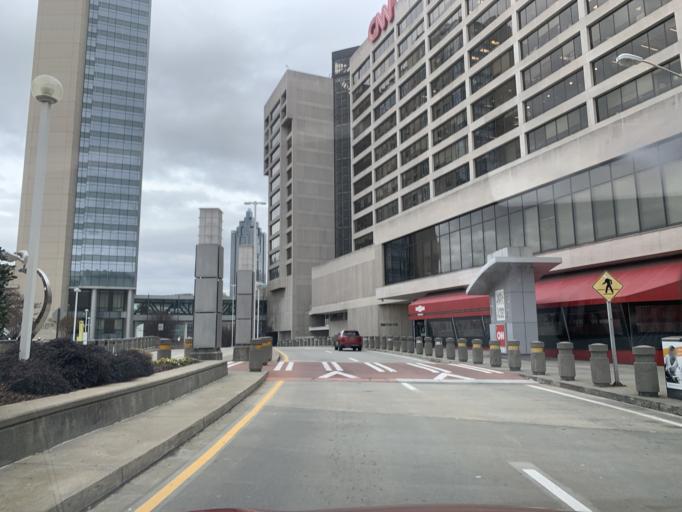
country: US
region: Georgia
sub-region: Fulton County
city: Atlanta
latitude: 33.7581
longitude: -84.3959
